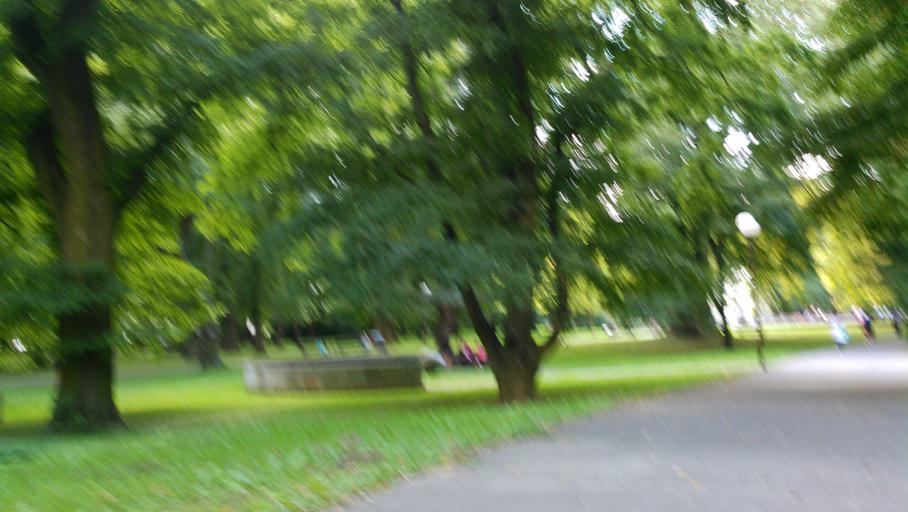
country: SK
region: Bratislavsky
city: Bratislava
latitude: 48.1337
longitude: 17.1132
